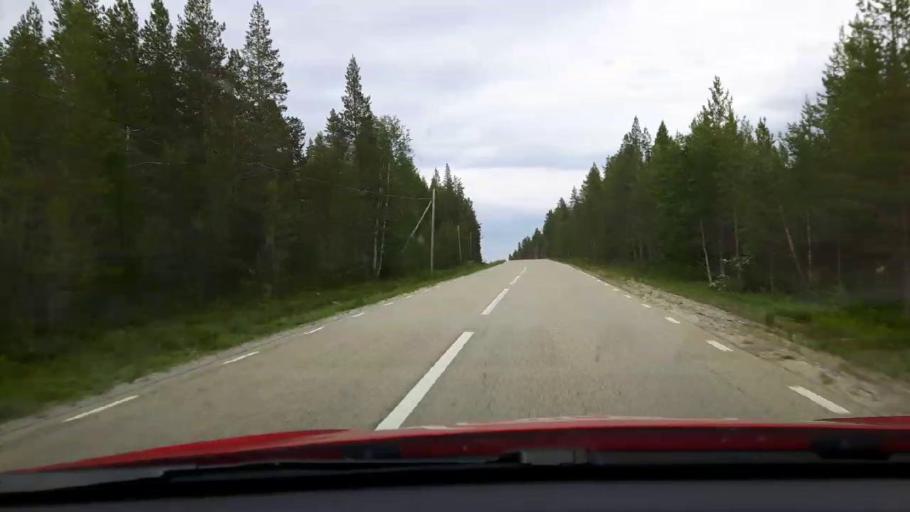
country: SE
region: Jaemtland
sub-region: Bergs Kommun
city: Hoverberg
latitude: 62.6490
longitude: 14.0781
